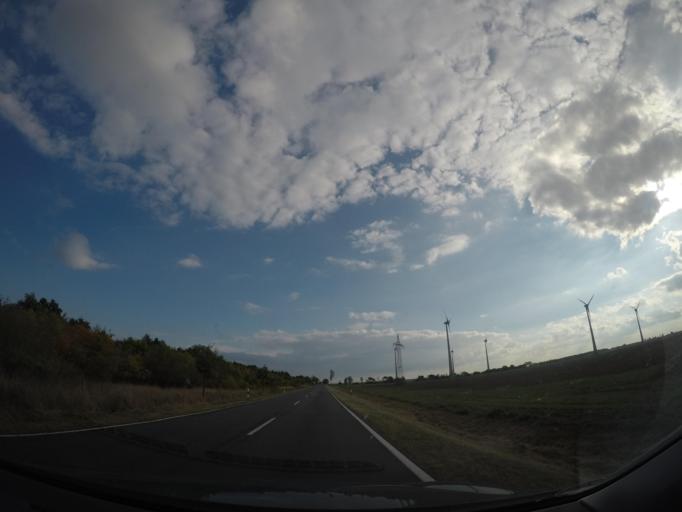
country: DE
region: Saxony-Anhalt
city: Weferlingen
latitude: 52.3935
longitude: 11.1029
